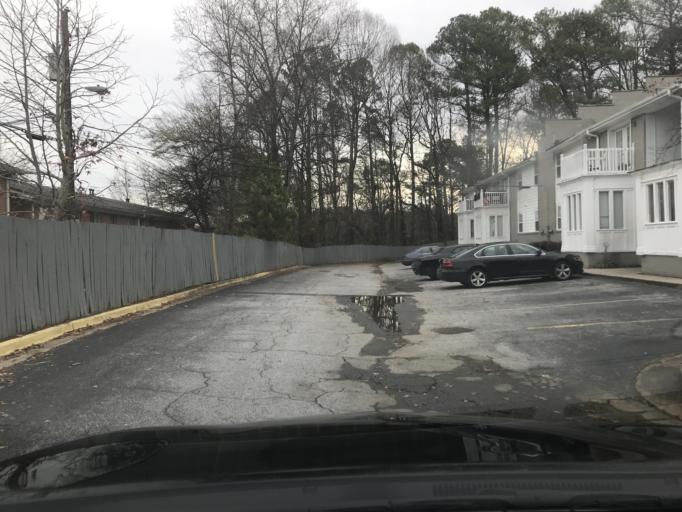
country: US
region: Georgia
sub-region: Fulton County
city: East Point
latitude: 33.7215
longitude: -84.5069
